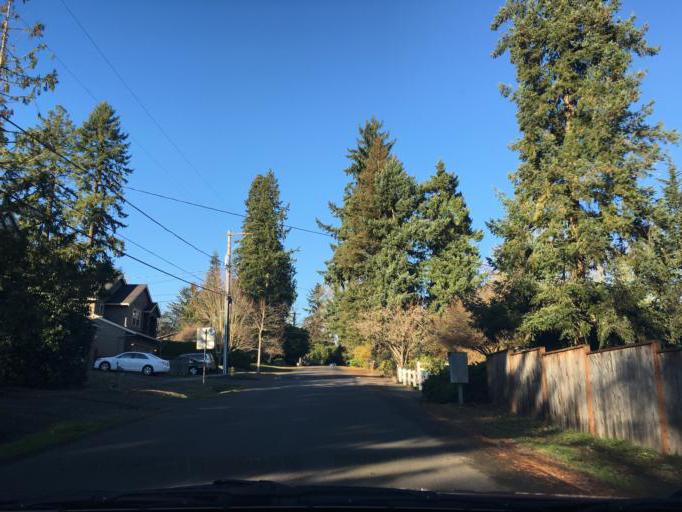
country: US
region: Oregon
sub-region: Washington County
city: West Slope
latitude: 45.4896
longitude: -122.7758
